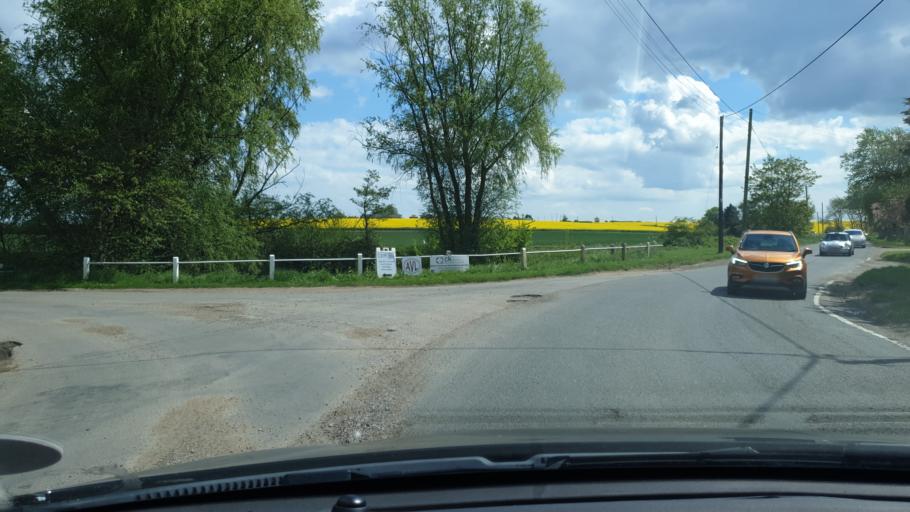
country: GB
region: England
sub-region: Essex
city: Little Clacton
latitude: 51.8645
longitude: 1.1836
